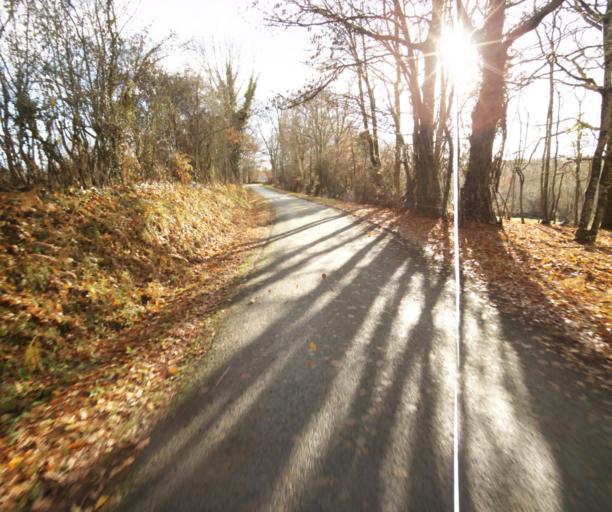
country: FR
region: Limousin
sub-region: Departement de la Correze
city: Sainte-Fereole
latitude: 45.2550
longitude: 1.6072
